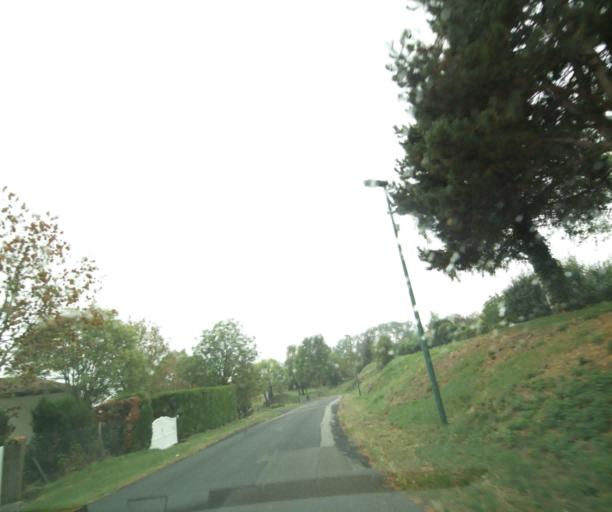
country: FR
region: Auvergne
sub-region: Departement du Puy-de-Dome
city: Ceyrat
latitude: 45.7244
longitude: 3.0455
